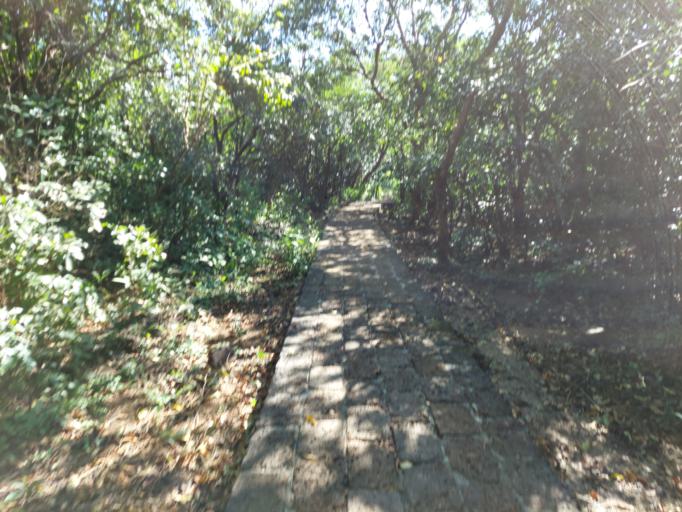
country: IN
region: Maharashtra
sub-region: Sindhudurg
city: Kudal
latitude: 16.0819
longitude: 73.8467
